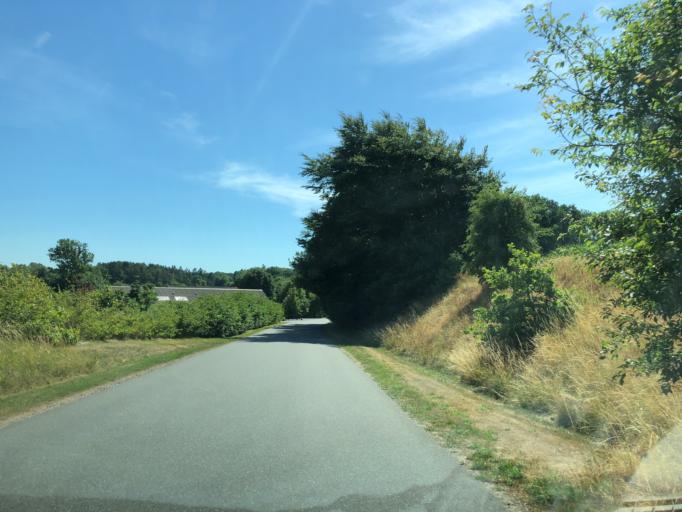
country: DK
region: Central Jutland
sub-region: Holstebro Kommune
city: Vinderup
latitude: 56.4181
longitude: 8.9315
